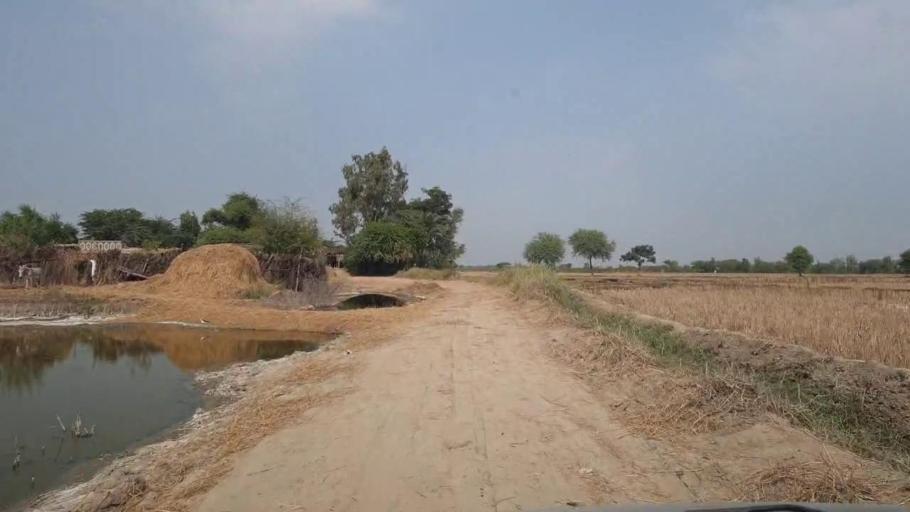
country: PK
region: Sindh
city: Matli
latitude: 24.9848
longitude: 68.7049
